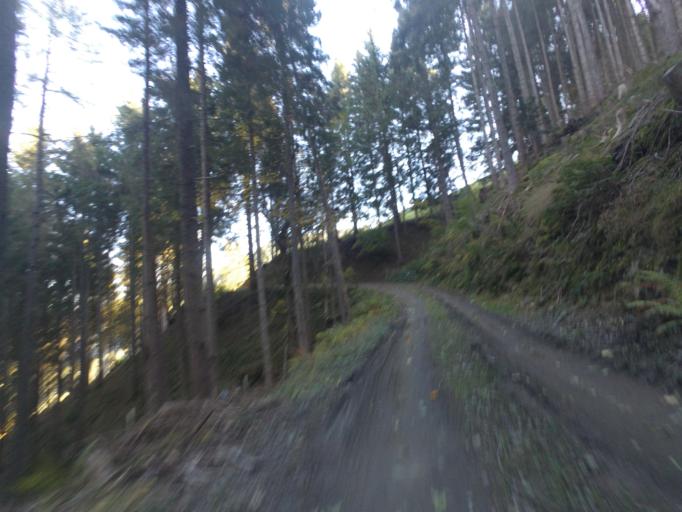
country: AT
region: Salzburg
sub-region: Politischer Bezirk Sankt Johann im Pongau
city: Sankt Johann im Pongau
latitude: 47.3270
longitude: 13.2273
